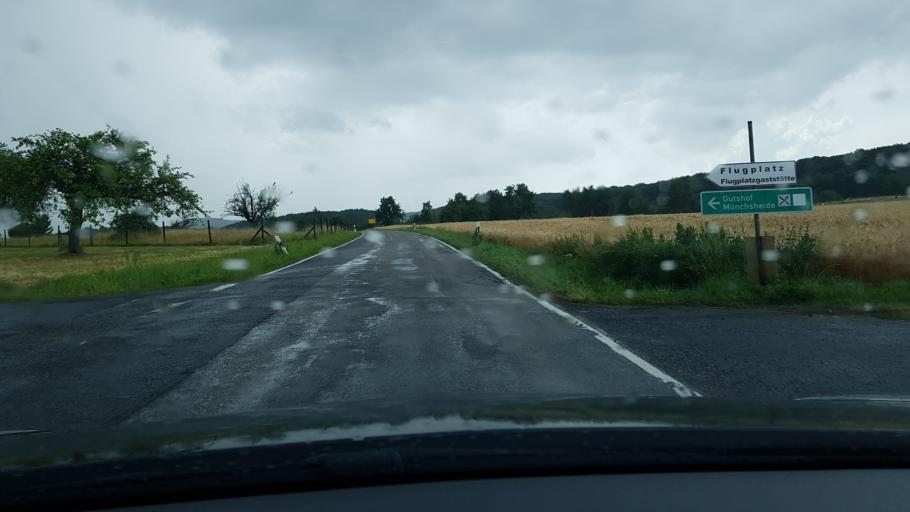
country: DE
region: Rheinland-Pfalz
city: Waldorf
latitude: 50.5042
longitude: 7.2299
